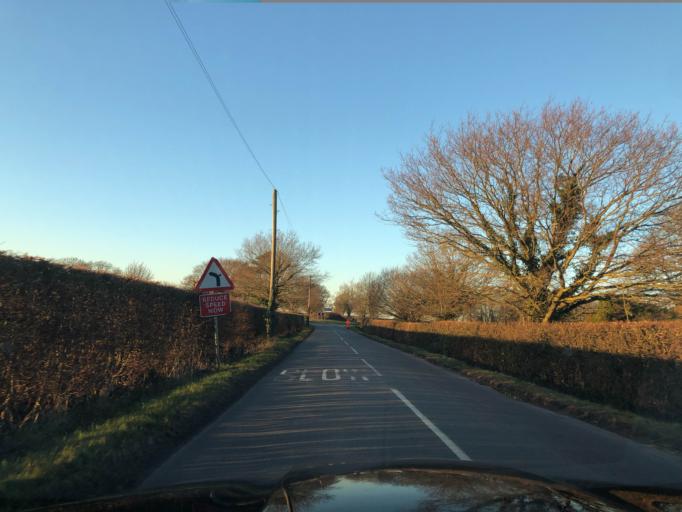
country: GB
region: England
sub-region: Warwickshire
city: Harbury
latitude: 52.2246
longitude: -1.4531
